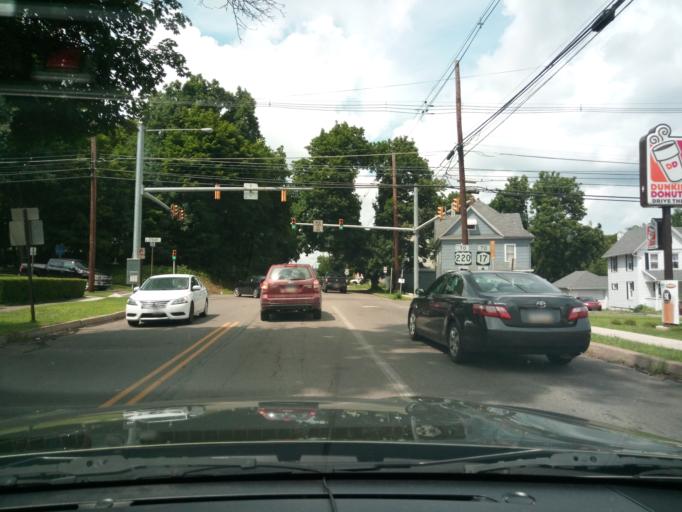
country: US
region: Pennsylvania
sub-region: Bradford County
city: Sayre
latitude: 41.9829
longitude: -76.5266
